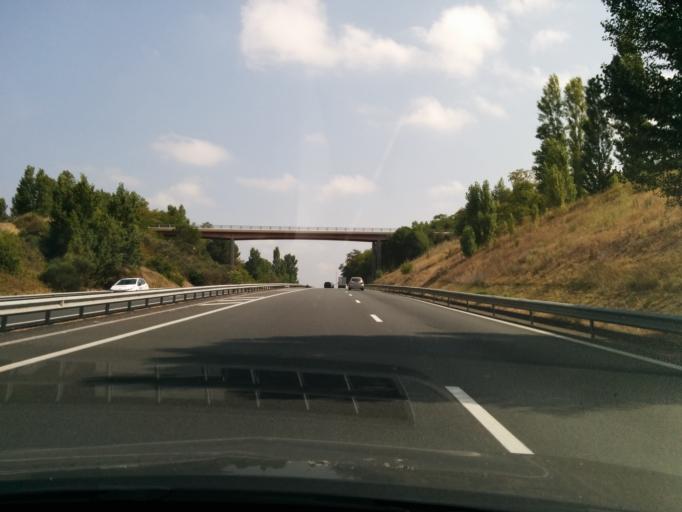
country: FR
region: Midi-Pyrenees
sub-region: Departement de la Haute-Garonne
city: Garidech
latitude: 43.7231
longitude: 1.5697
